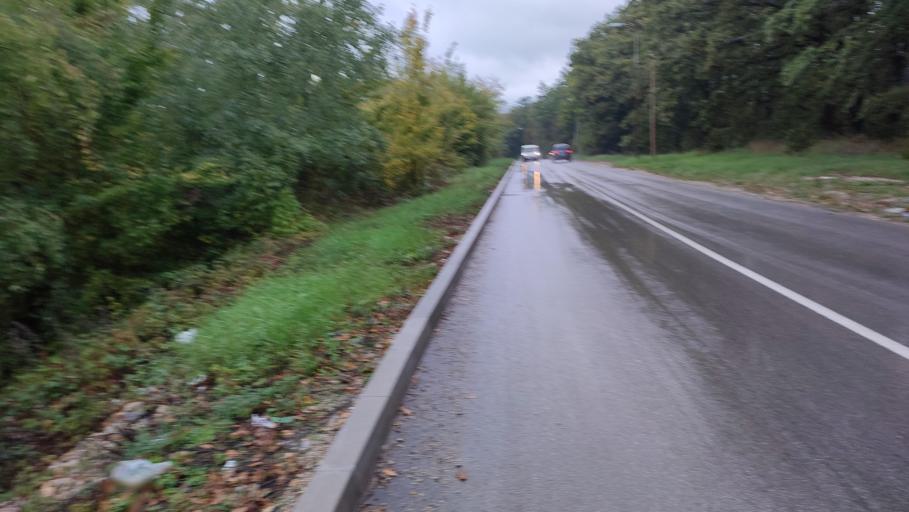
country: RS
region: Central Serbia
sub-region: Zlatiborski Okrug
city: Uzice
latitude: 43.8585
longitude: 19.8609
